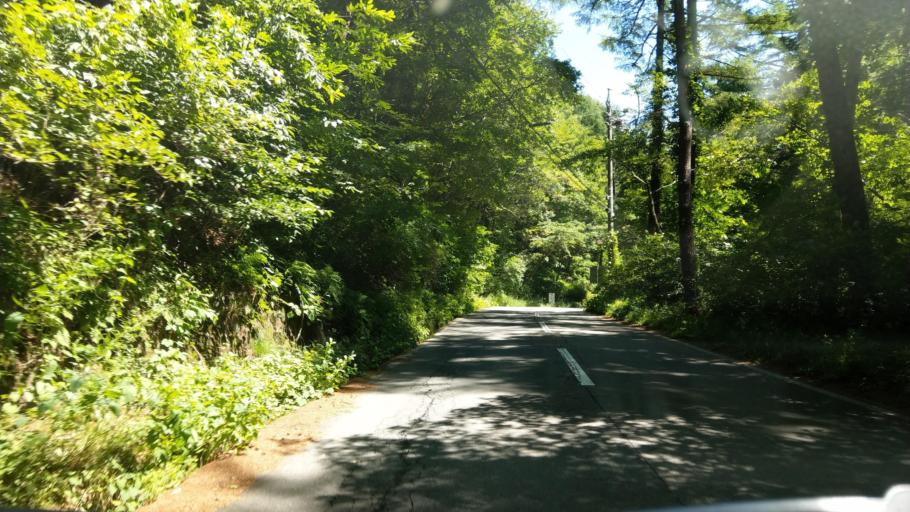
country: JP
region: Nagano
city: Komoro
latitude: 36.3727
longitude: 138.4609
